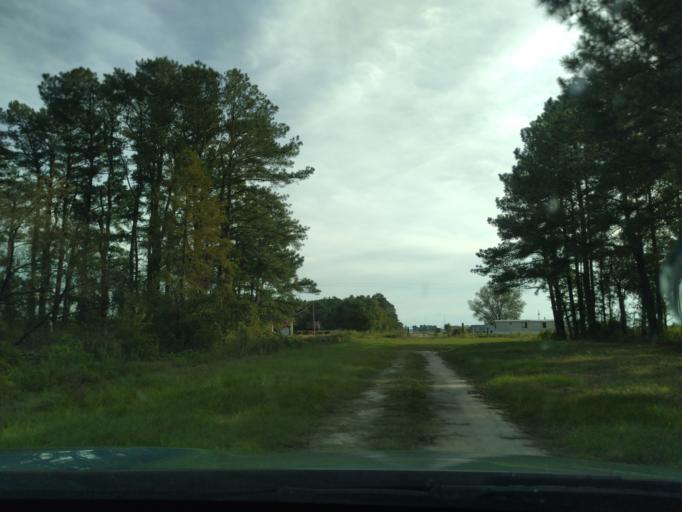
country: US
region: North Carolina
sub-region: Beaufort County
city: Belhaven
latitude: 35.6612
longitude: -76.5499
